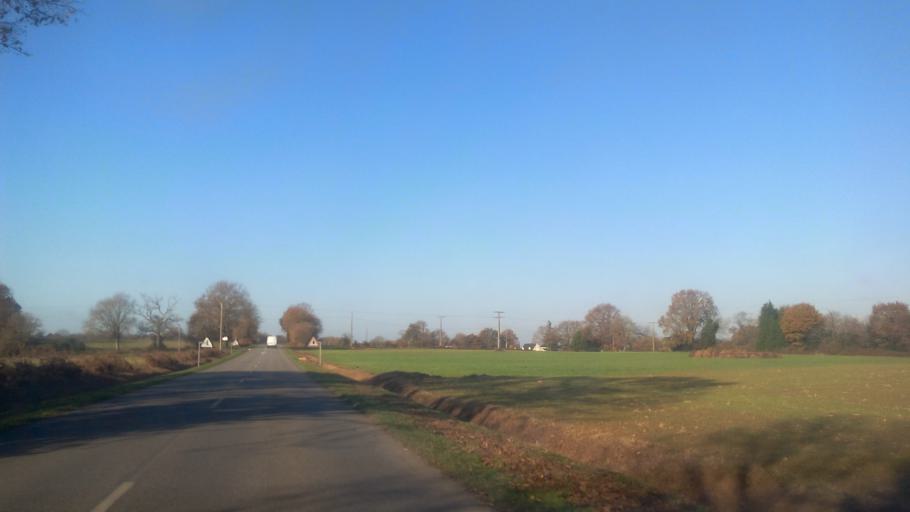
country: FR
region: Brittany
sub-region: Departement du Morbihan
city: Saint-Vincent-sur-Oust
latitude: 47.7111
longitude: -2.1736
